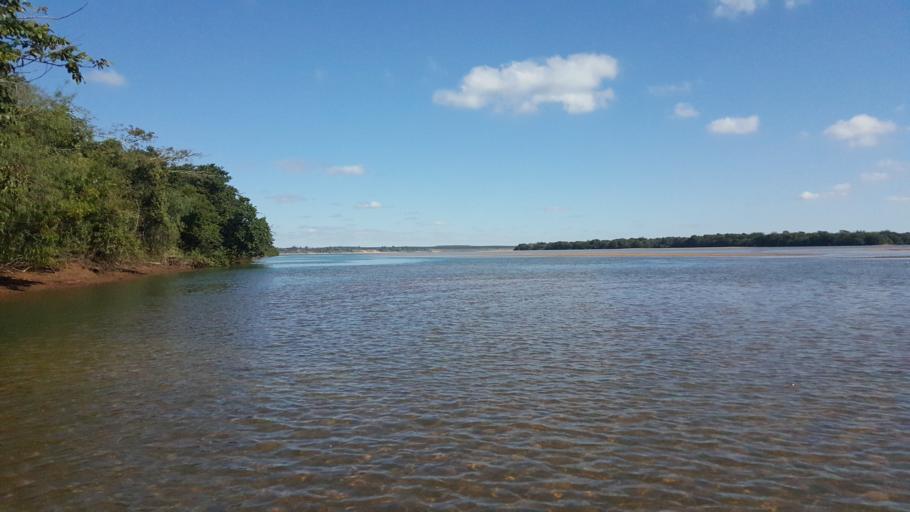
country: AR
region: Corrientes
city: Ituzaingo
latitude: -27.5777
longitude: -56.7089
